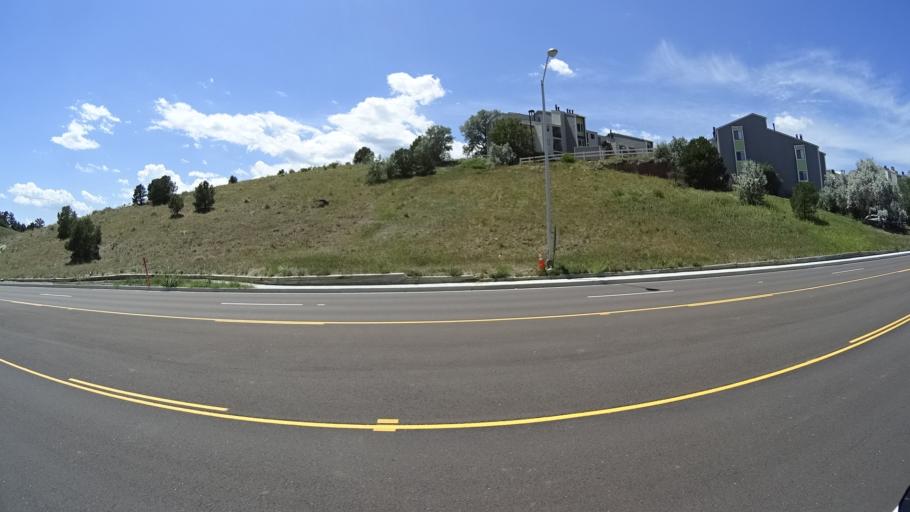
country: US
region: Colorado
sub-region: El Paso County
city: Colorado Springs
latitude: 38.9160
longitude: -104.8309
